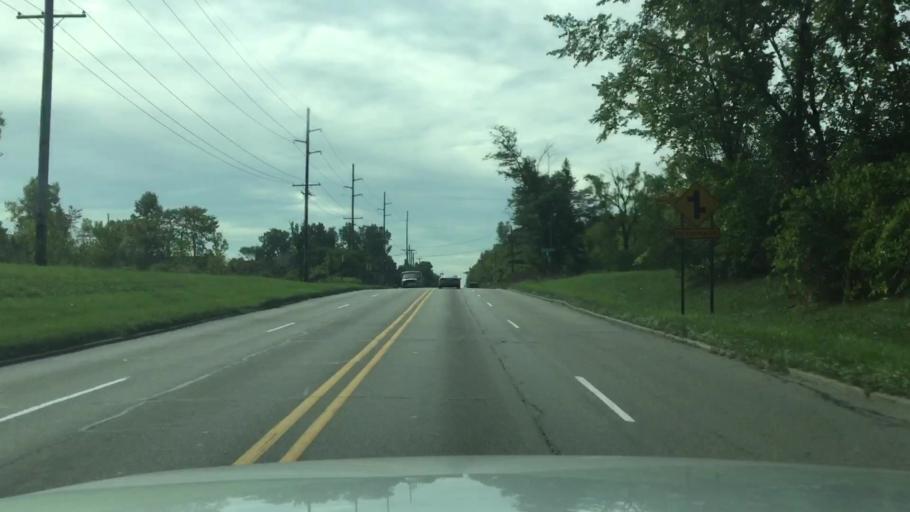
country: US
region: Michigan
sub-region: Wayne County
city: Canton
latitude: 42.2606
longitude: -83.4868
